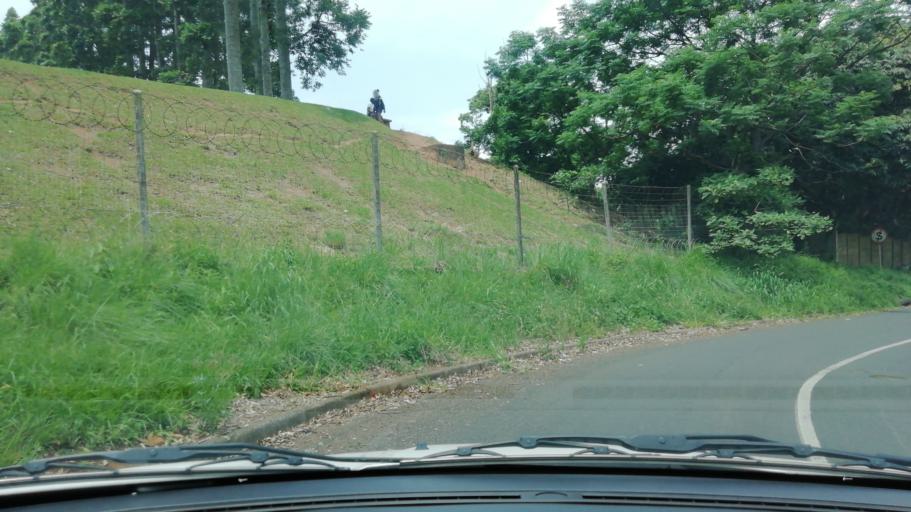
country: ZA
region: KwaZulu-Natal
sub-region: uThungulu District Municipality
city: Empangeni
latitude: -28.7500
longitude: 31.8922
